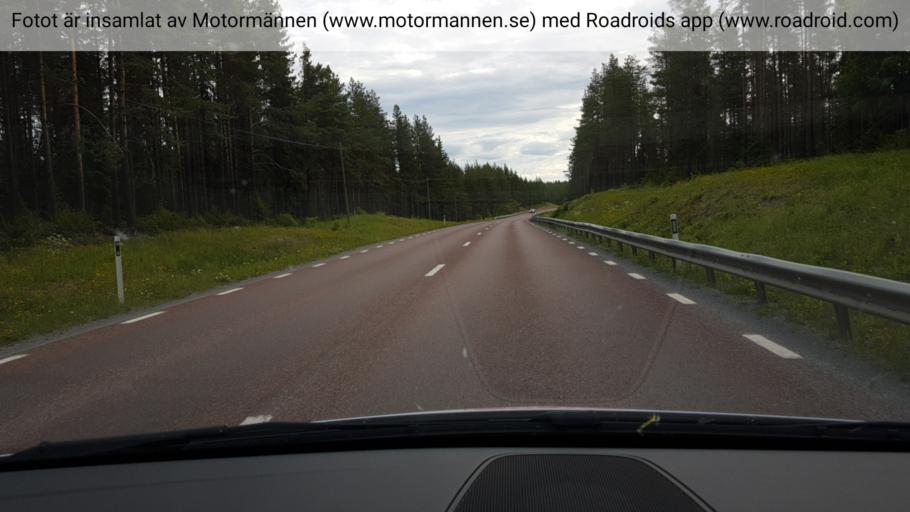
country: SE
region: Jaemtland
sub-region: OEstersunds Kommun
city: Ostersund
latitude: 62.9951
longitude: 14.6138
